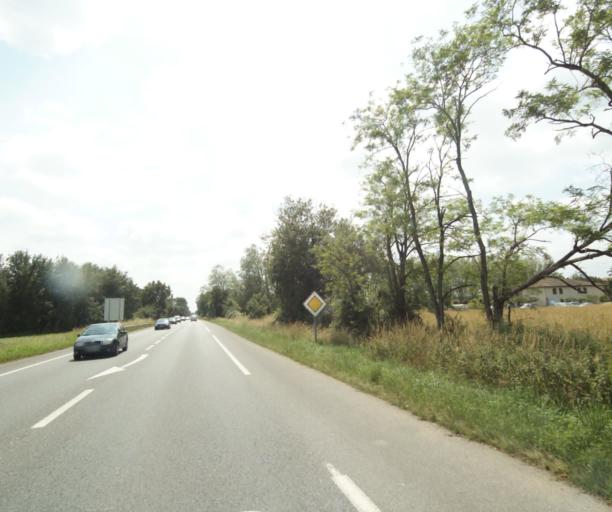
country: FR
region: Midi-Pyrenees
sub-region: Departement du Tarn-et-Garonne
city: Albias
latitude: 44.0748
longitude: 1.4274
